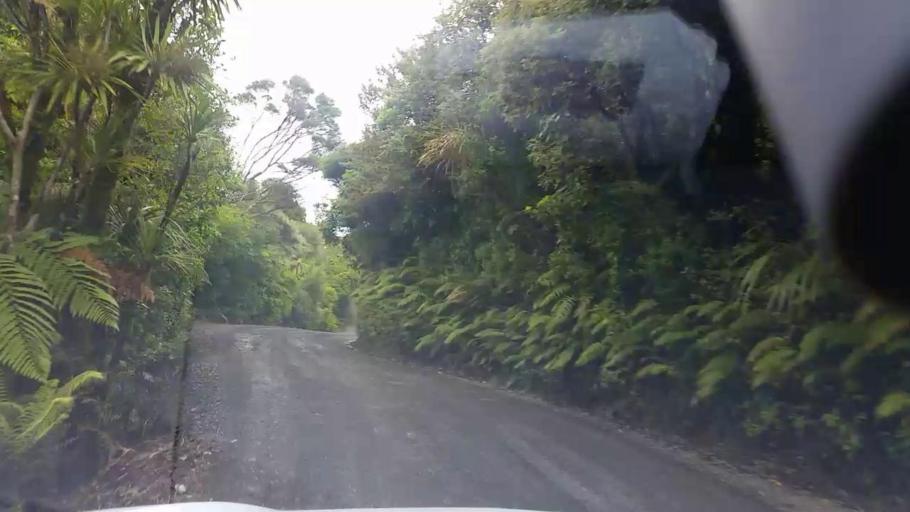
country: NZ
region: Auckland
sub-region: Auckland
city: Titirangi
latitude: -36.9412
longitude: 174.5222
